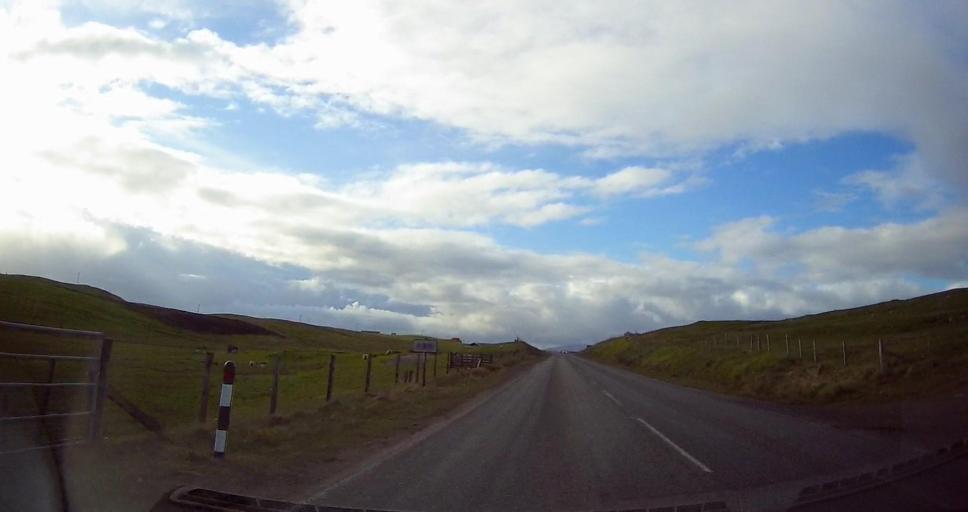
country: GB
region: Scotland
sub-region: Shetland Islands
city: Lerwick
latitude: 60.3741
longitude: -1.3373
